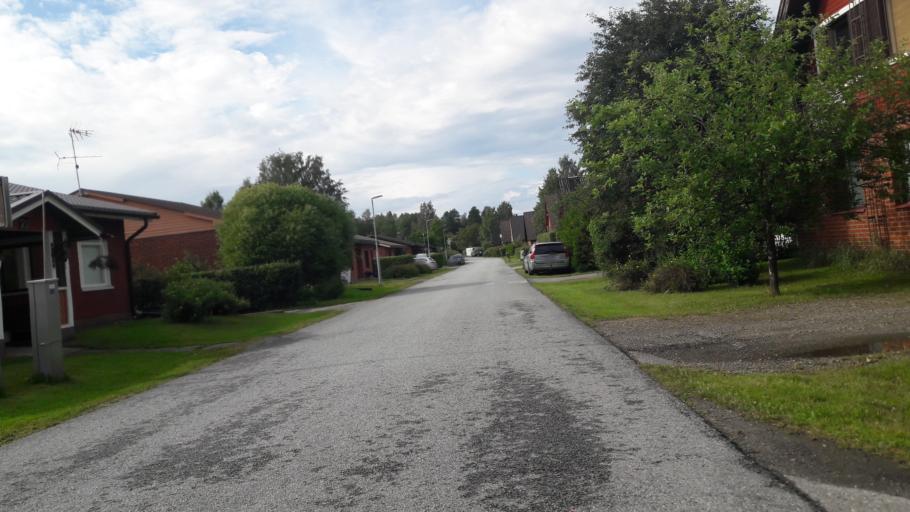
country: FI
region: North Karelia
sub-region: Joensuu
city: Joensuu
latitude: 62.5795
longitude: 29.8114
